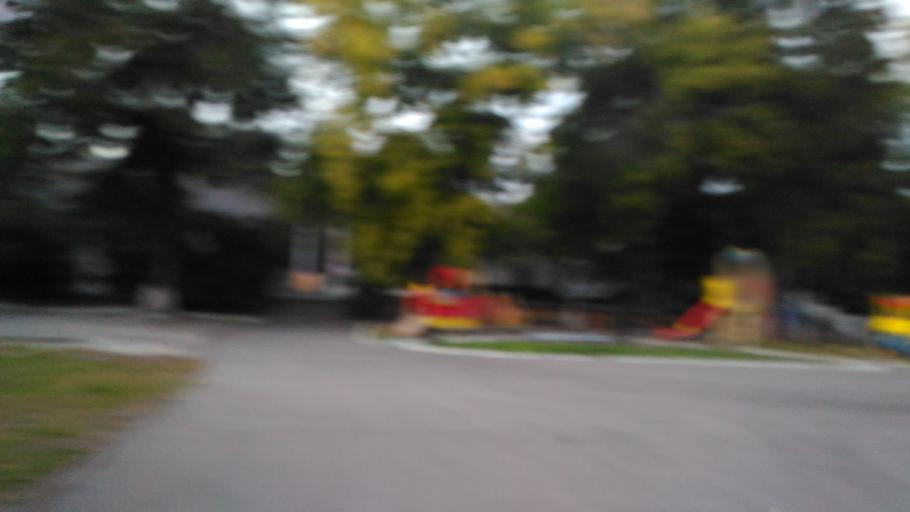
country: RU
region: Ulyanovsk
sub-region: Ulyanovskiy Rayon
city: Ulyanovsk
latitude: 54.3113
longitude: 48.4035
